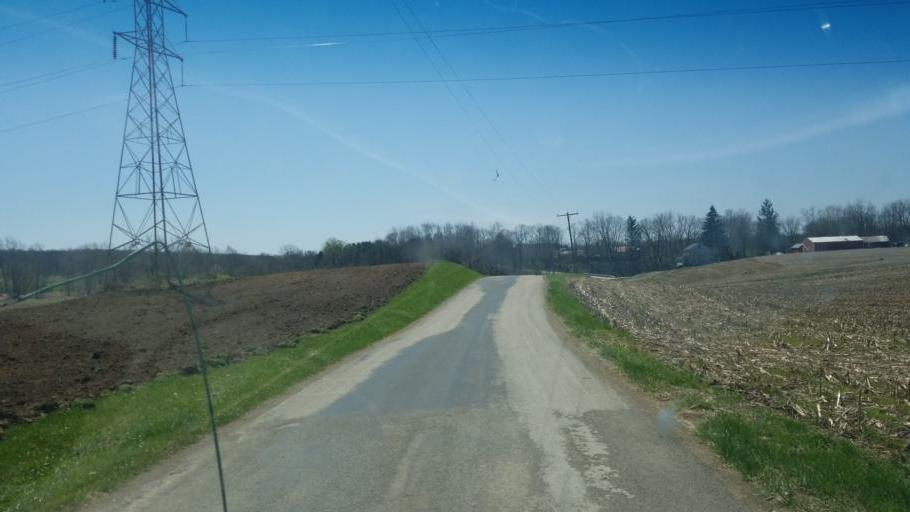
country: US
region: Ohio
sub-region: Richland County
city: Lincoln Heights
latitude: 40.8528
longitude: -82.4210
